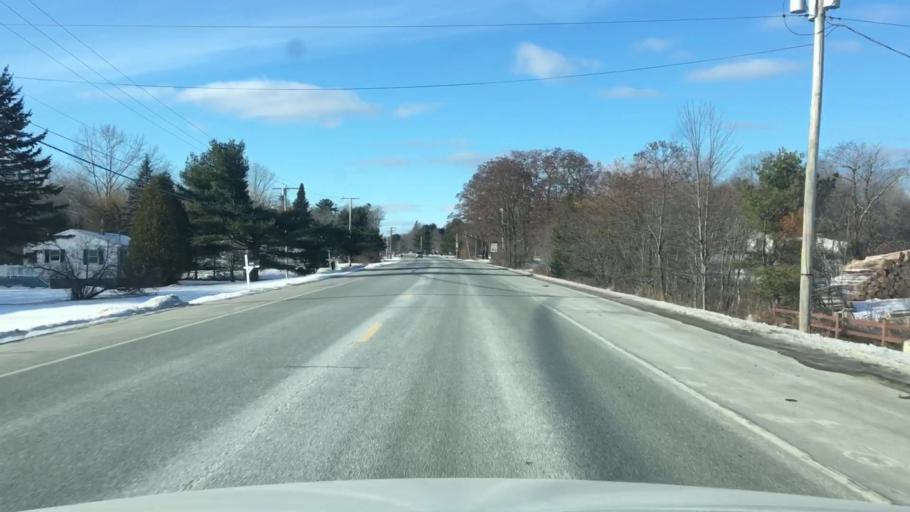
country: US
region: Maine
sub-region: Penobscot County
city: Eddington
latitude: 44.8252
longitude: -68.6543
